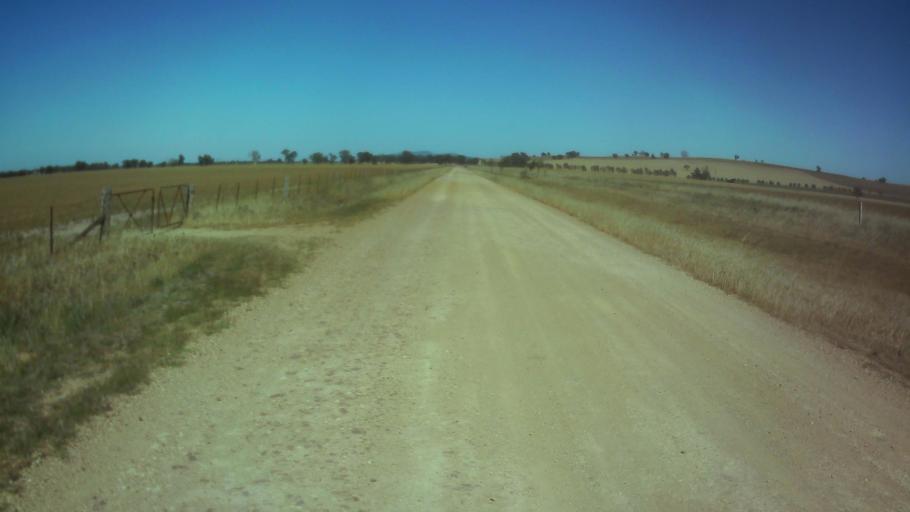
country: AU
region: New South Wales
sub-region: Weddin
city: Grenfell
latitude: -33.9957
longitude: 148.3707
